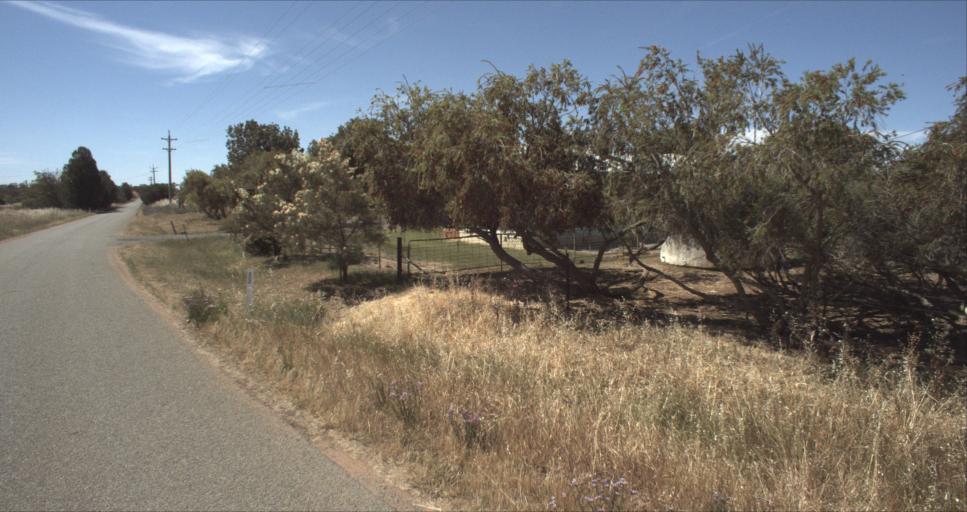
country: AU
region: New South Wales
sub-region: Leeton
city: Leeton
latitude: -34.5951
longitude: 146.4401
